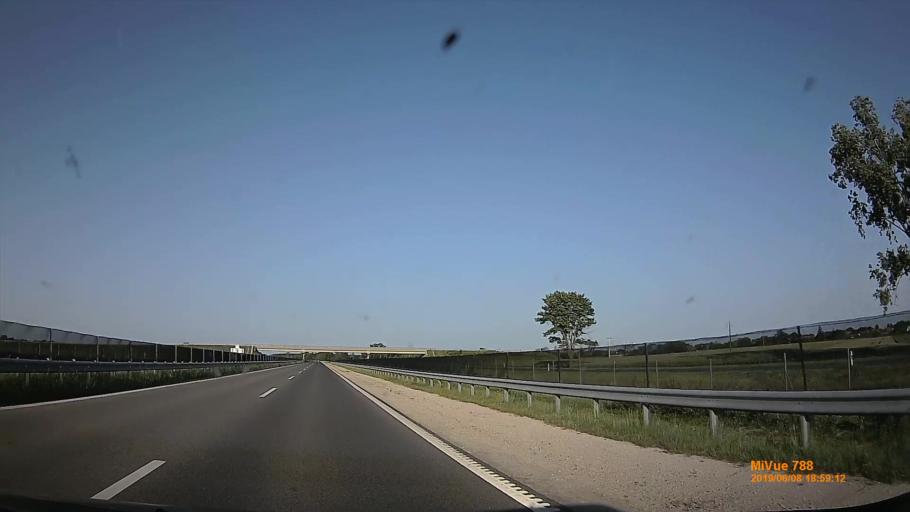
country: HU
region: Gyor-Moson-Sopron
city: Kony
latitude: 47.6388
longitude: 17.3675
